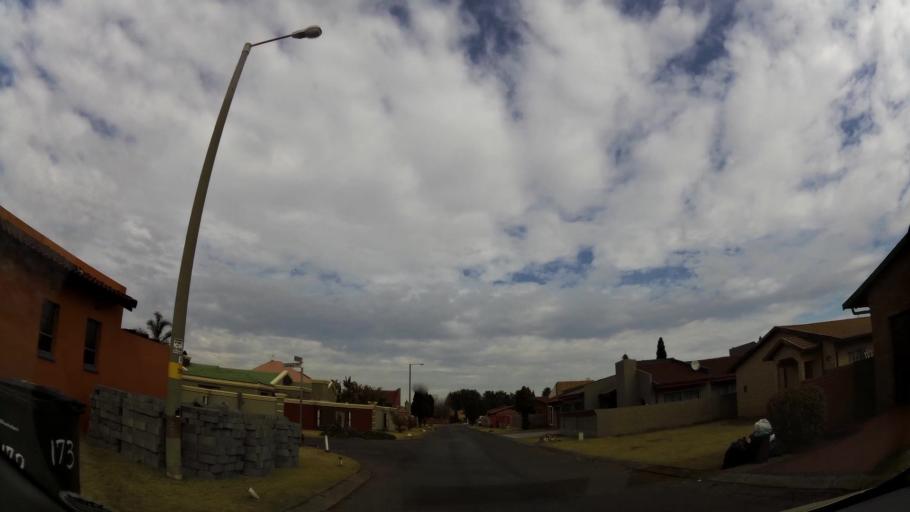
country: ZA
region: Gauteng
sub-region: Ekurhuleni Metropolitan Municipality
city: Germiston
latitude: -26.3222
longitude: 28.1861
